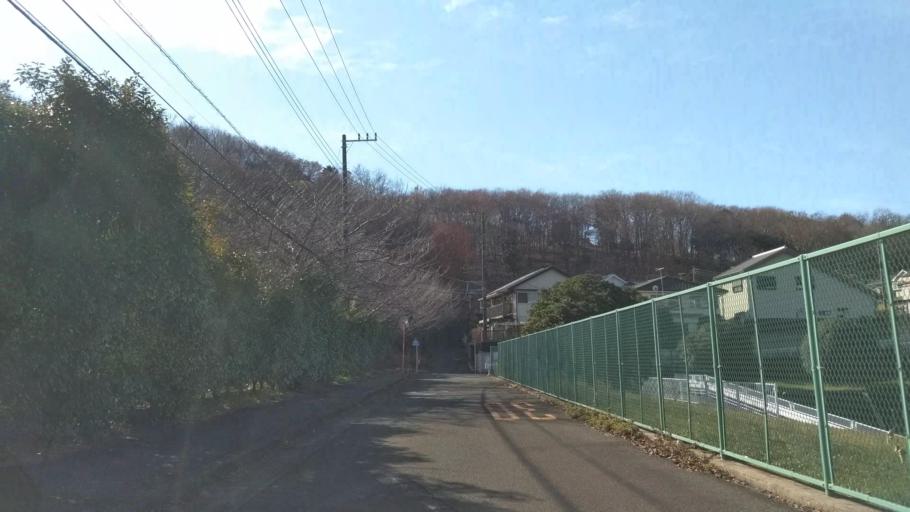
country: JP
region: Kanagawa
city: Hadano
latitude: 35.3574
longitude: 139.2312
